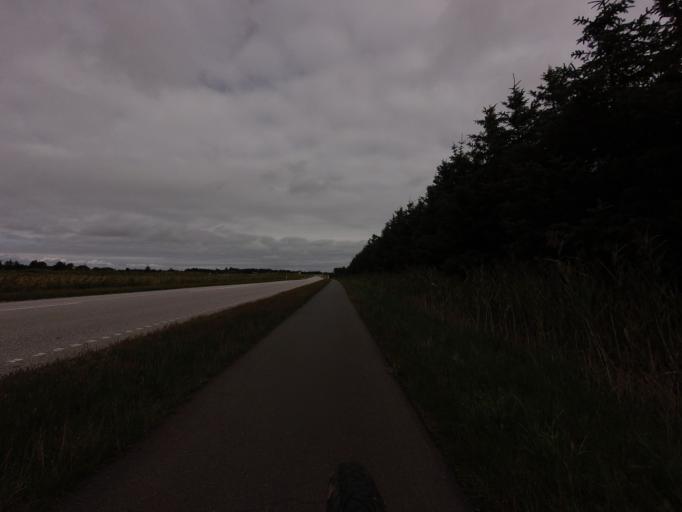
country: DK
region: North Denmark
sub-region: Hjorring Kommune
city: Hirtshals
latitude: 57.5569
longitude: 9.9391
